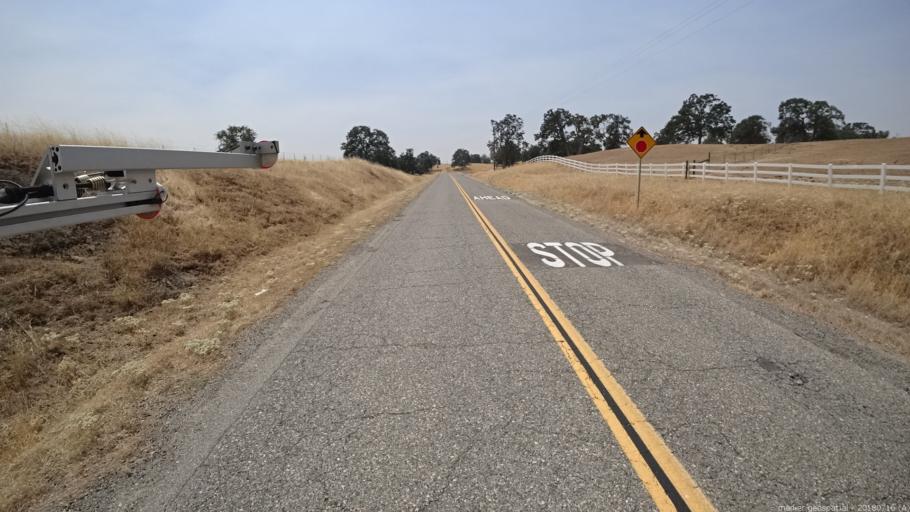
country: US
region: California
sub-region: Madera County
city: Bonadelle Ranchos-Madera Ranchos
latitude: 37.1068
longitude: -119.8888
